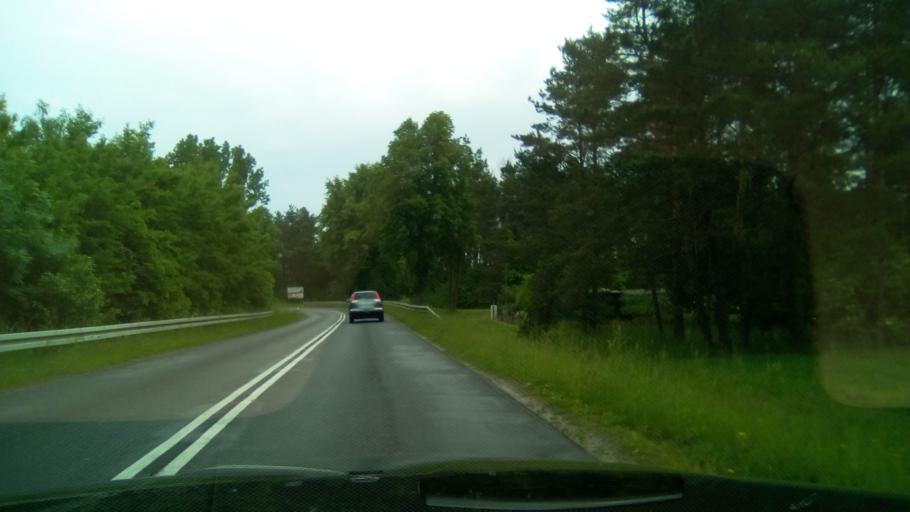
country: PL
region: Kujawsko-Pomorskie
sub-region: Powiat sepolenski
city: Wiecbork
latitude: 53.3709
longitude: 17.4989
